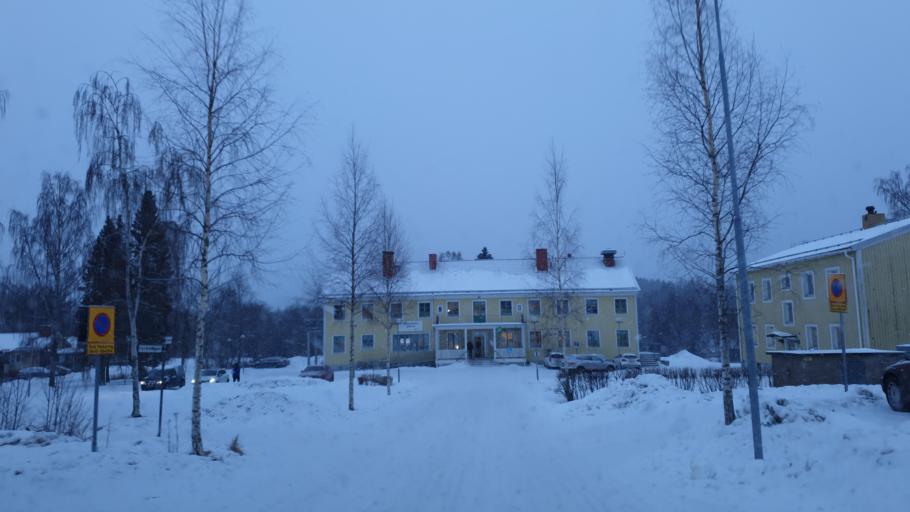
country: SE
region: Vaesternorrland
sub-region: OErnskoeldsviks Kommun
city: Ornskoldsvik
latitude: 63.2926
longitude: 18.6176
